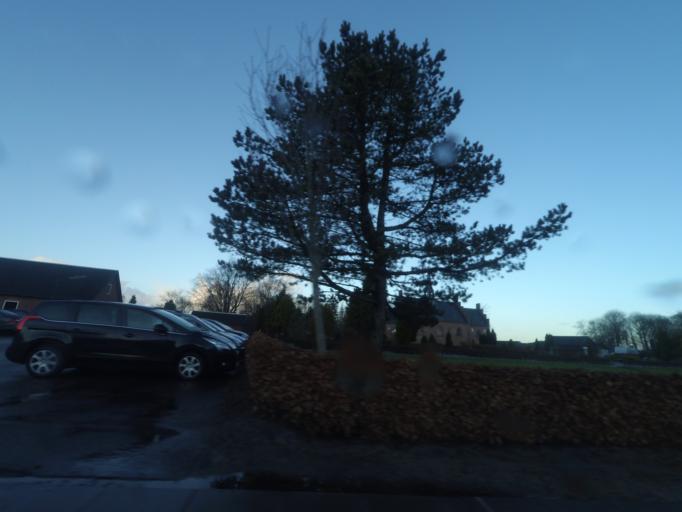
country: DK
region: Central Jutland
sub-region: Ikast-Brande Kommune
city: Brande
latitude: 56.0080
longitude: 9.1138
